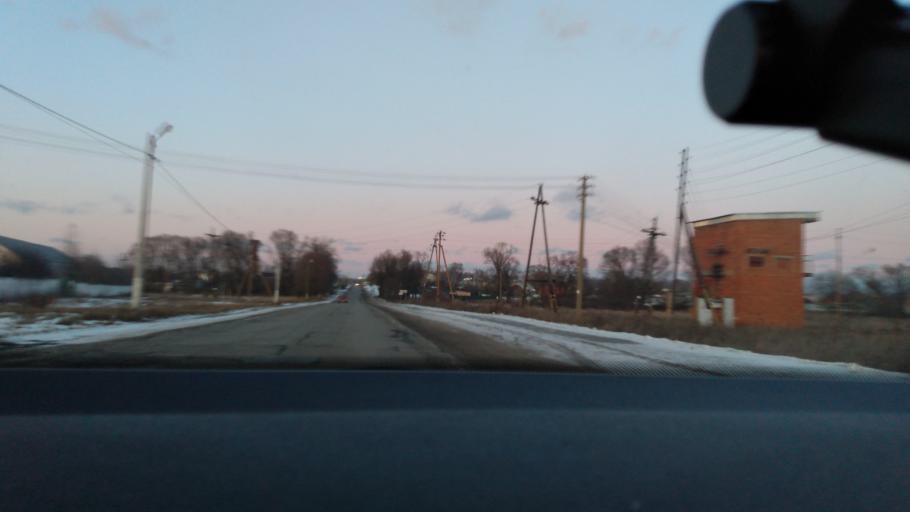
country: RU
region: Moskovskaya
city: Krasnaya Poyma
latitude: 55.1147
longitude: 39.0679
